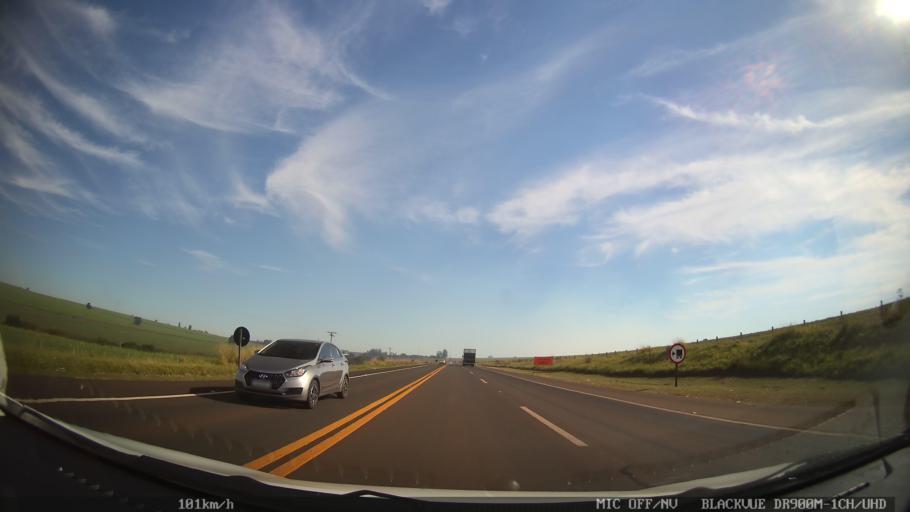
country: BR
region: Sao Paulo
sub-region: Americo Brasiliense
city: Americo Brasiliense
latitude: -21.7646
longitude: -48.0832
